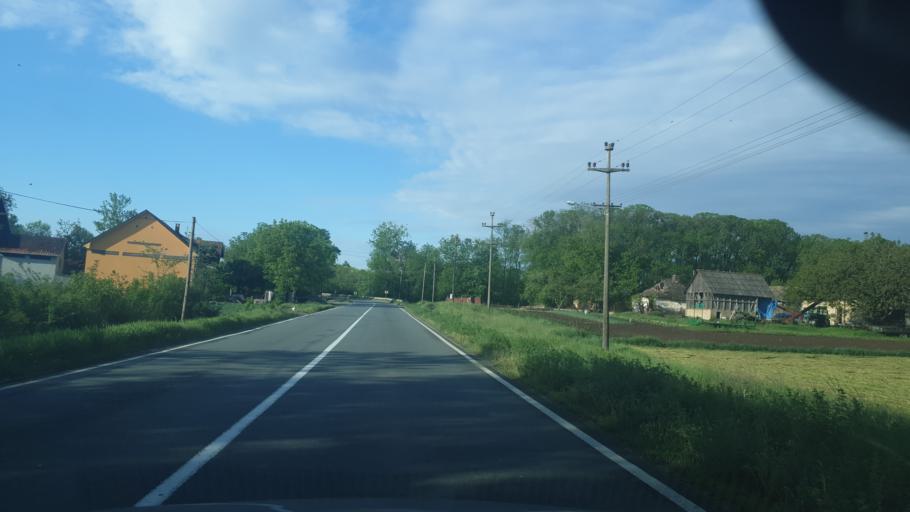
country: RS
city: Stubline
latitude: 44.5969
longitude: 20.1460
